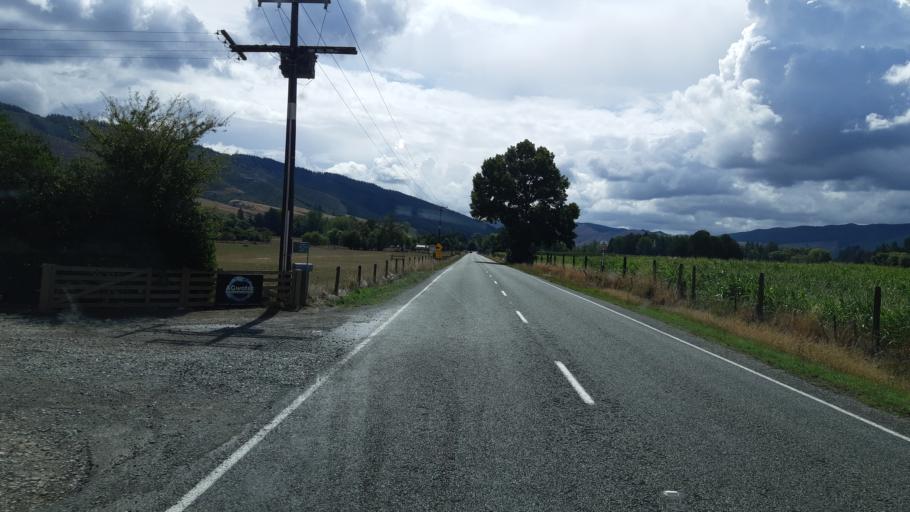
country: NZ
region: Tasman
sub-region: Tasman District
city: Wakefield
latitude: -41.4661
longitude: 172.8084
